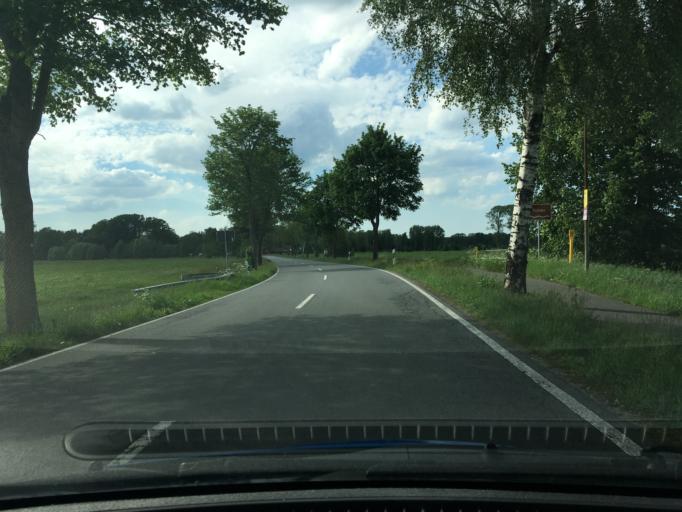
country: DE
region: Lower Saxony
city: Welle
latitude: 53.2434
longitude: 9.7974
